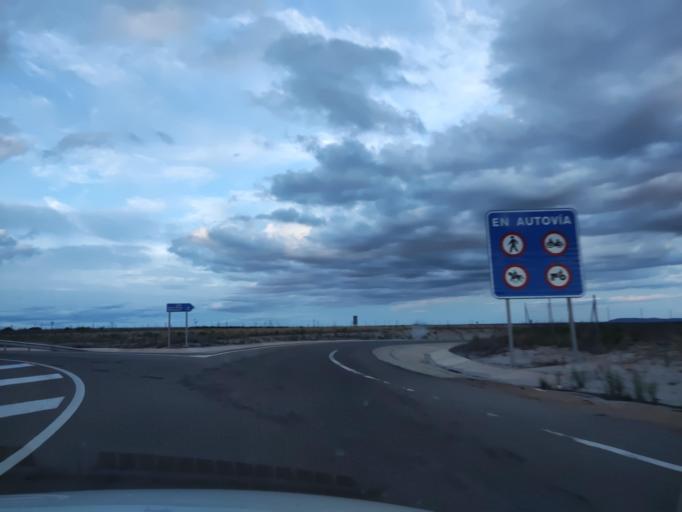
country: ES
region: Castille and Leon
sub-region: Provincia de Salamanca
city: Fuentes de Onoro
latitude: 40.5928
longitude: -6.7965
